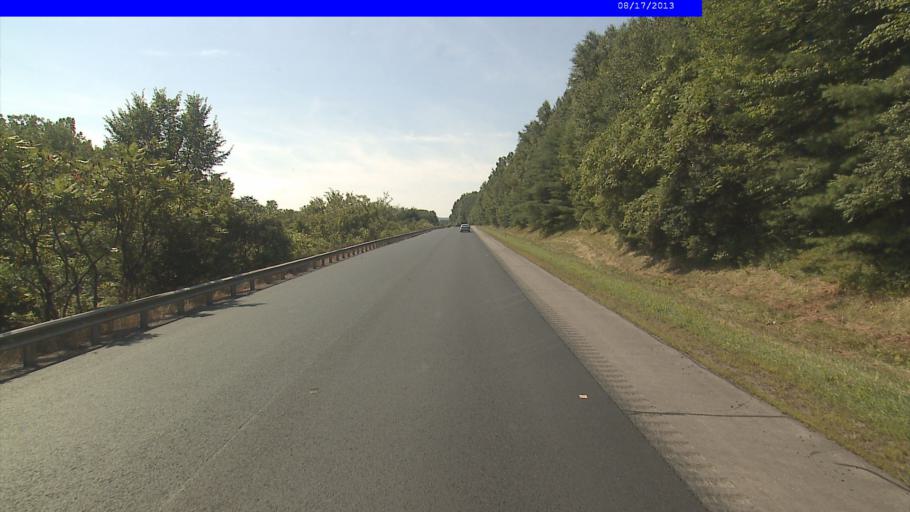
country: US
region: New Hampshire
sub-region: Cheshire County
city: Chesterfield
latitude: 42.9327
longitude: -72.5282
